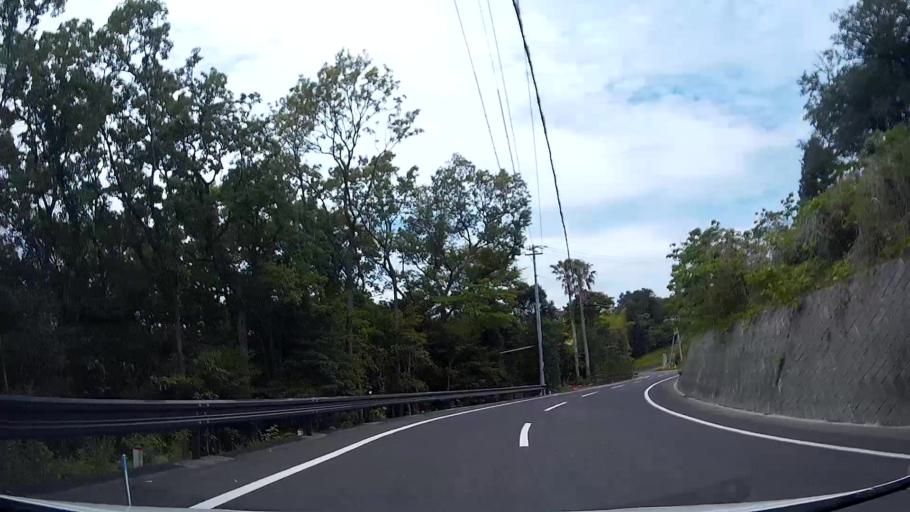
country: JP
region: Shizuoka
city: Ito
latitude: 34.9269
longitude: 139.1396
